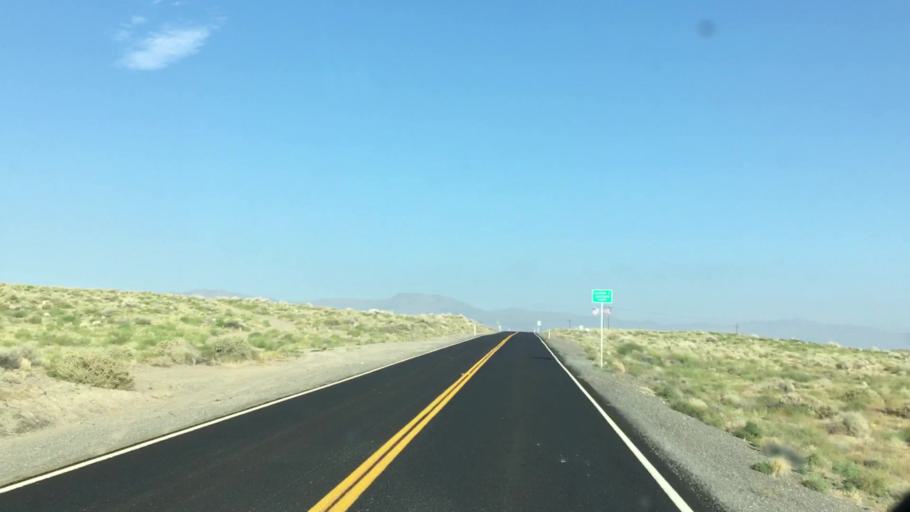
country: US
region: Nevada
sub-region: Lyon County
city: Fernley
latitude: 39.6393
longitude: -119.2943
